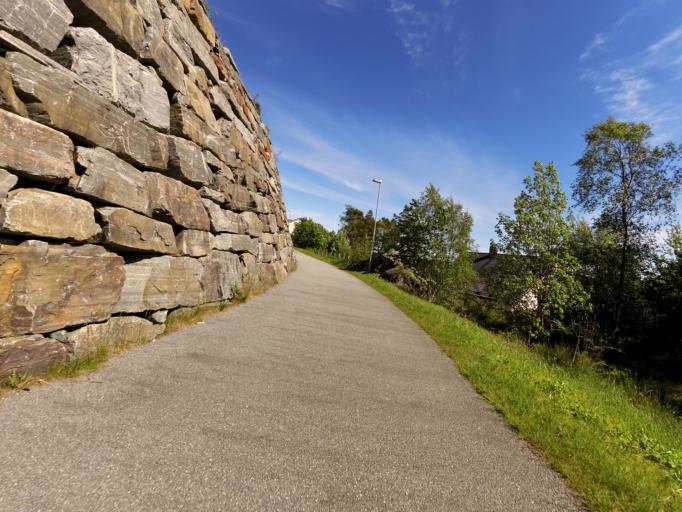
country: NO
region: Hordaland
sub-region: Stord
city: Sagvag
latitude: 59.7814
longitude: 5.3844
